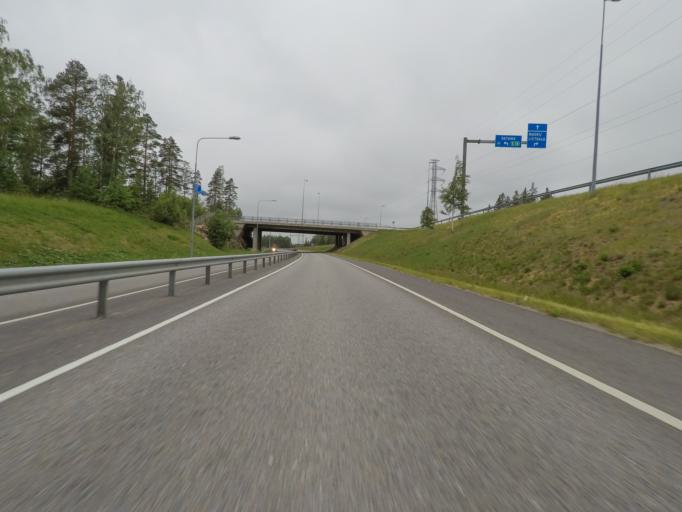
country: FI
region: Varsinais-Suomi
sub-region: Turku
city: Naantali
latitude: 60.4737
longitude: 22.0689
